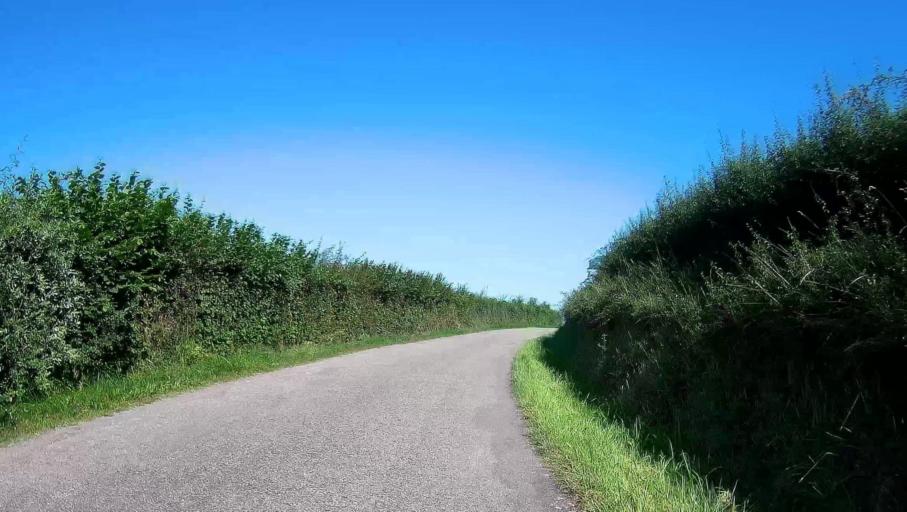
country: FR
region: Bourgogne
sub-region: Departement de Saone-et-Loire
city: Saint-Leger-sur-Dheune
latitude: 46.8275
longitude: 4.5945
